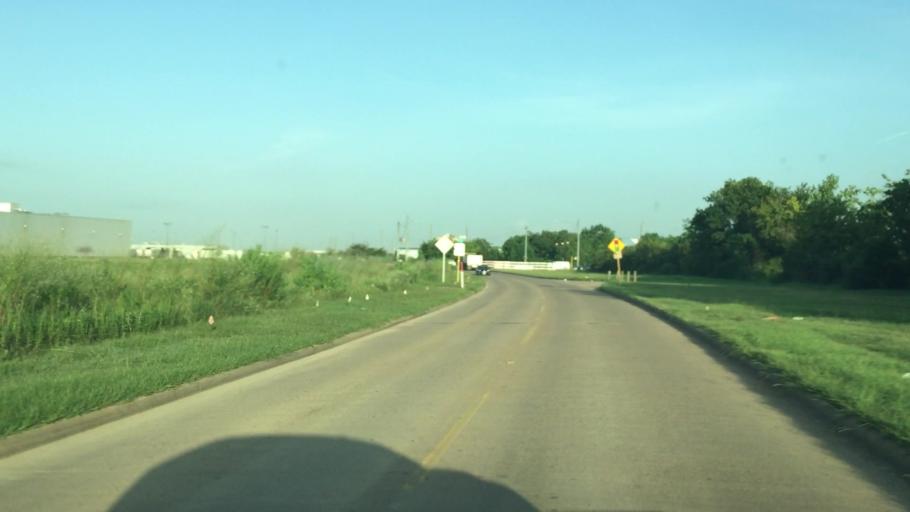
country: US
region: Texas
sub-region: Harris County
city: Hudson
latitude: 29.9430
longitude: -95.4814
